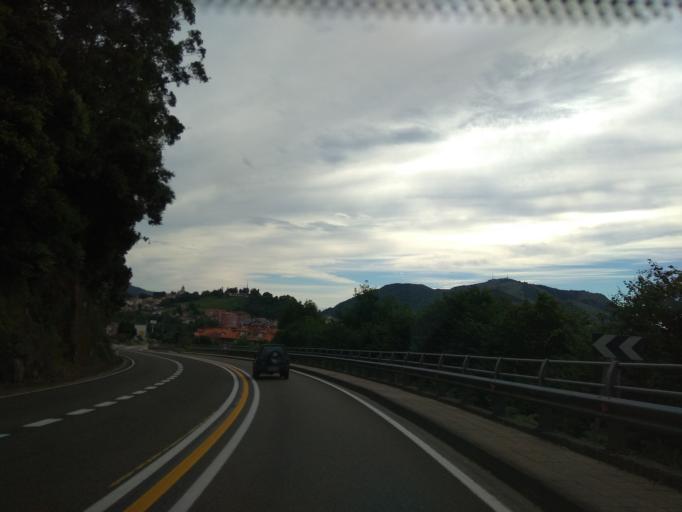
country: ES
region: Cantabria
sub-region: Provincia de Cantabria
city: Entrambasaguas
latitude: 43.3888
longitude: -3.7242
